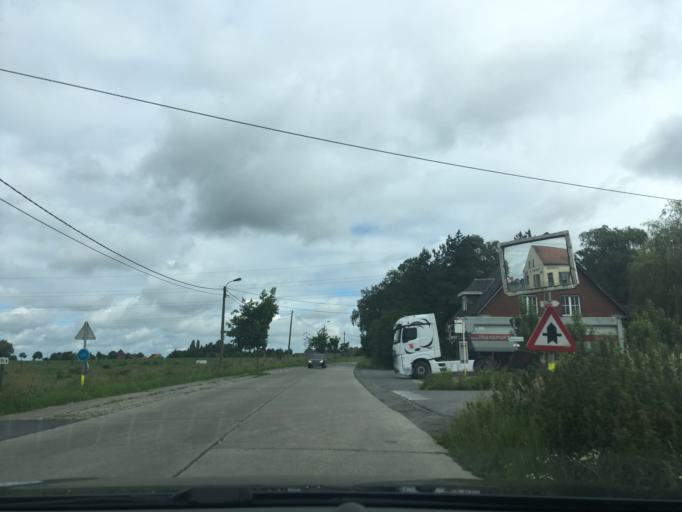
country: BE
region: Flanders
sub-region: Provincie West-Vlaanderen
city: Hooglede
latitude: 50.9558
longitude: 3.0579
